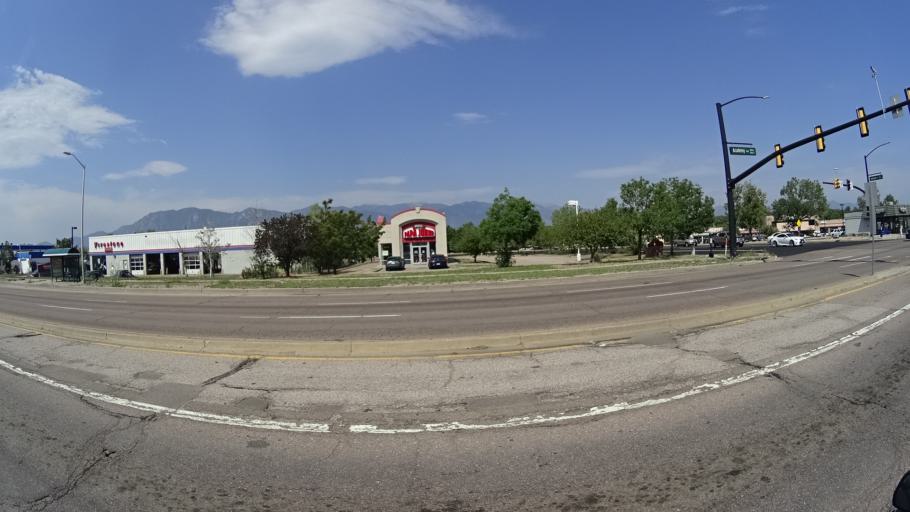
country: US
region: Colorado
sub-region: El Paso County
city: Stratmoor
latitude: 38.7961
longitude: -104.7575
